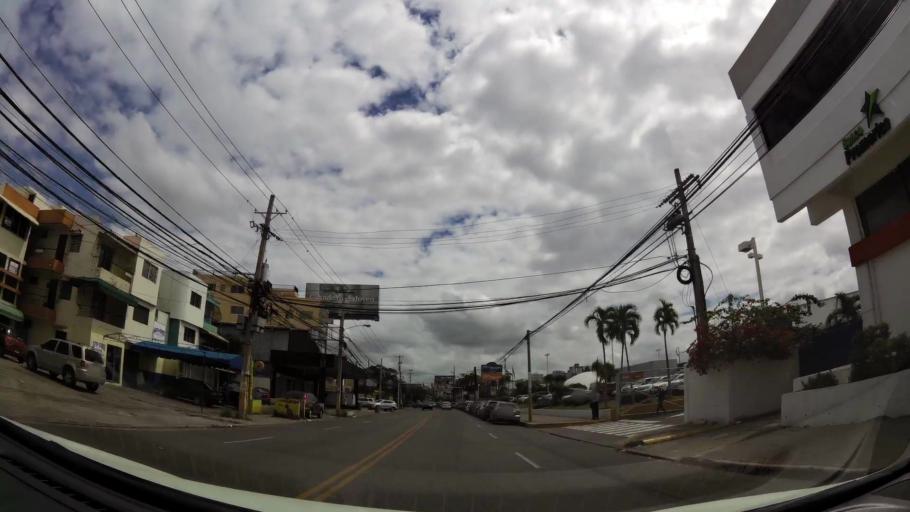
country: DO
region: Nacional
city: La Julia
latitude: 18.4771
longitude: -69.9508
